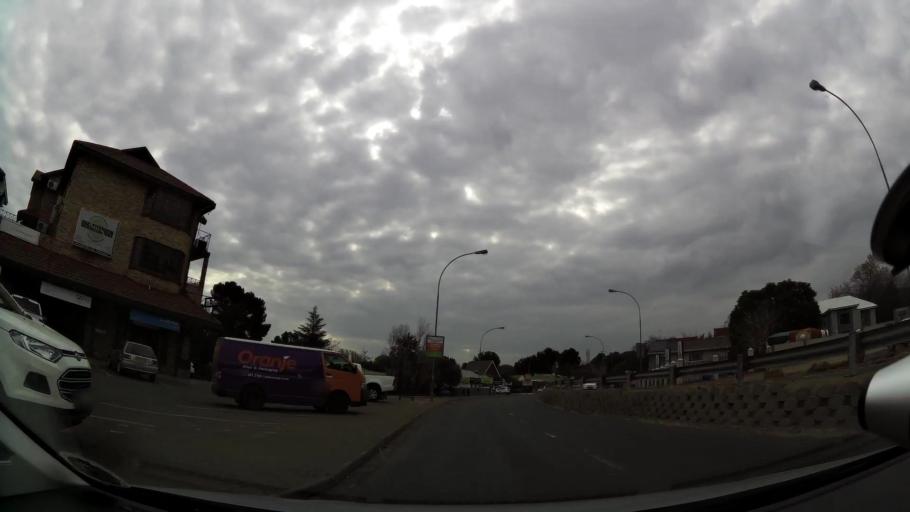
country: ZA
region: Orange Free State
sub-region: Mangaung Metropolitan Municipality
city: Bloemfontein
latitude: -29.1077
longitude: 26.2134
